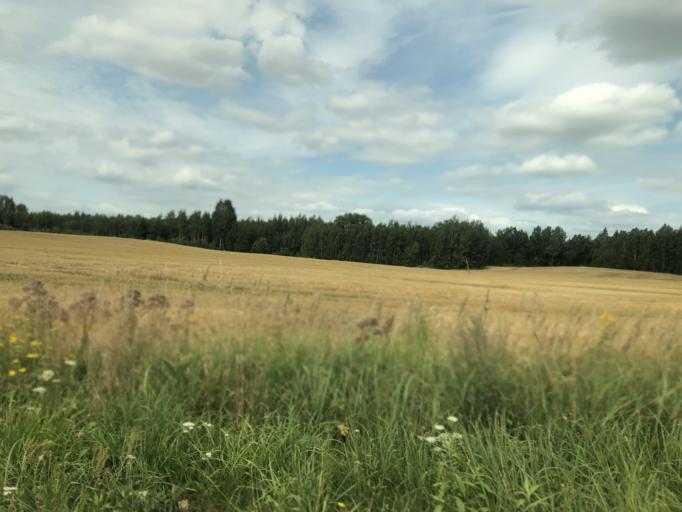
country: LV
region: Vecumnieki
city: Vecumnieki
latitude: 56.4561
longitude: 24.6478
